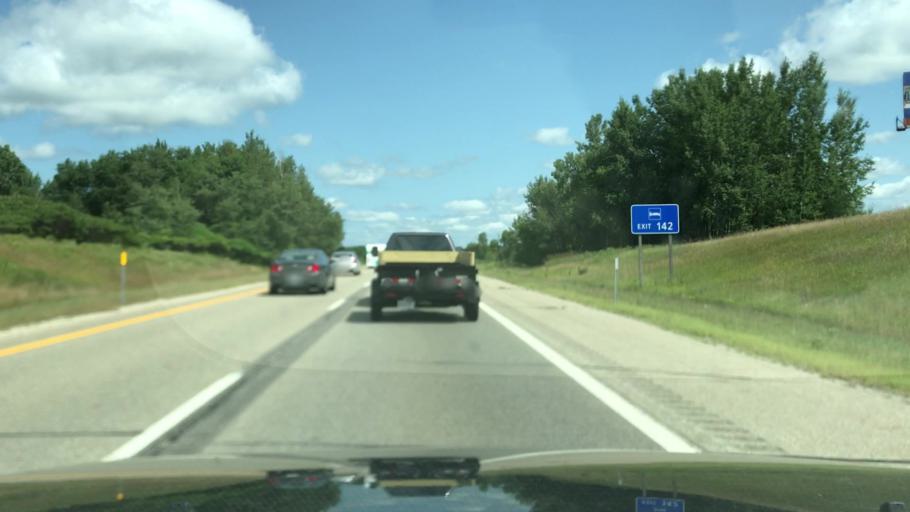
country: US
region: Michigan
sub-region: Mecosta County
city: Big Rapids
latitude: 43.7244
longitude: -85.5319
